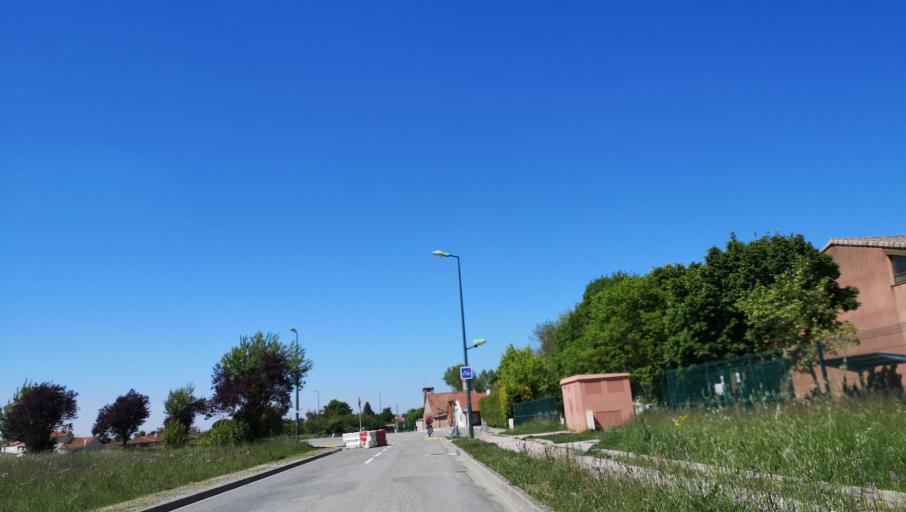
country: FR
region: Midi-Pyrenees
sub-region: Departement de la Haute-Garonne
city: Beauzelle
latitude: 43.6785
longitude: 1.3675
